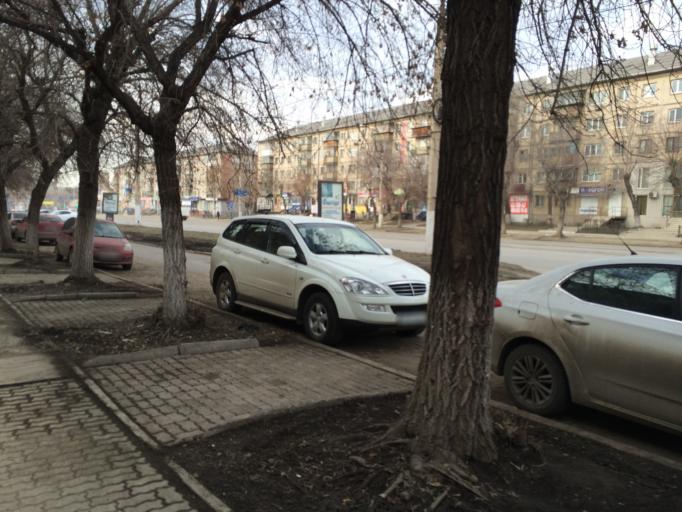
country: RU
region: Chelyabinsk
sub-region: Gorod Magnitogorsk
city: Magnitogorsk
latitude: 53.4009
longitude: 58.9785
